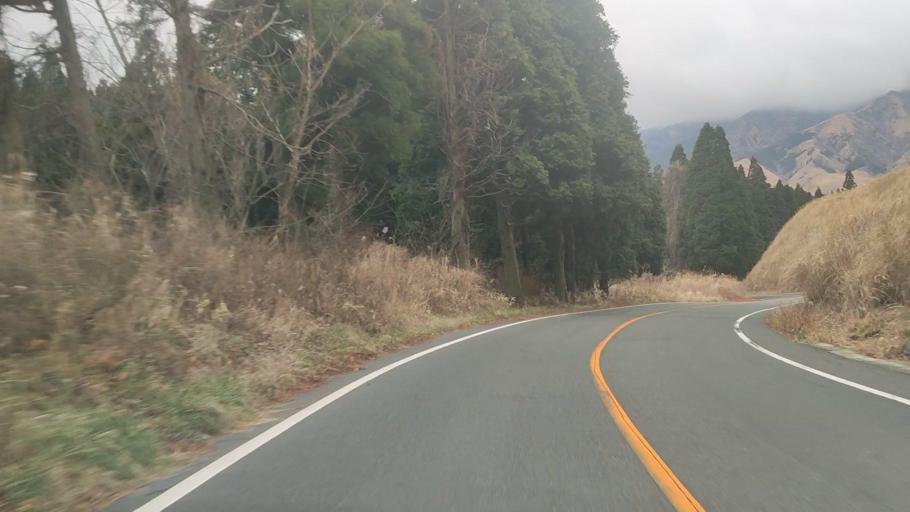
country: JP
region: Kumamoto
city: Aso
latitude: 32.9097
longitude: 131.1426
